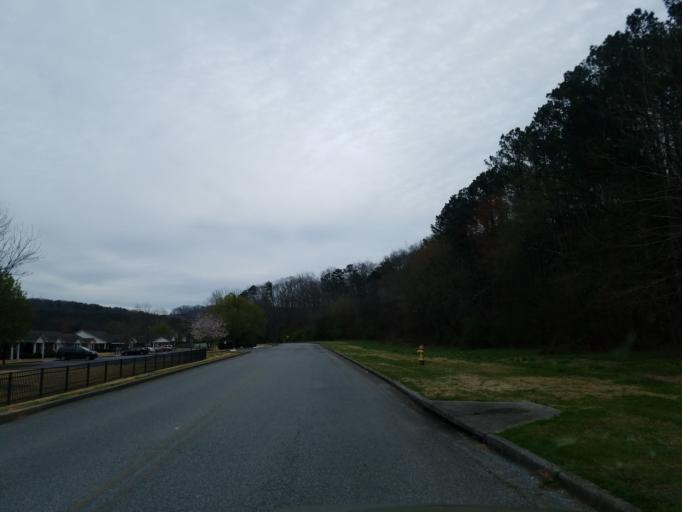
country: US
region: Georgia
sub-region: Bartow County
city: Cartersville
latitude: 34.2145
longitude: -84.7833
